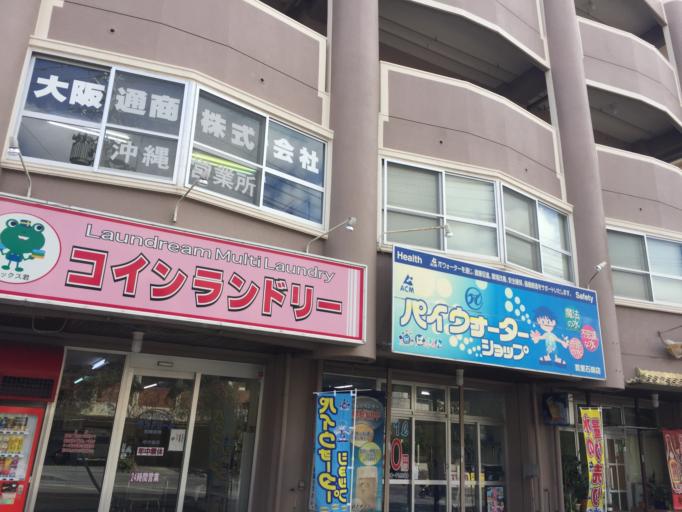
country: JP
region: Okinawa
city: Ginowan
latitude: 26.2344
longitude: 127.7292
